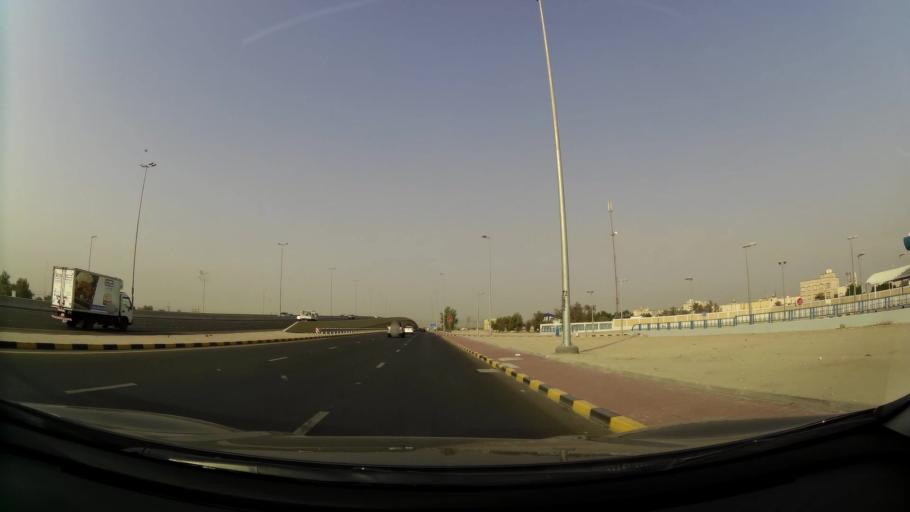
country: KW
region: Al Asimah
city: Ar Rabiyah
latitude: 29.3117
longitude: 47.8110
